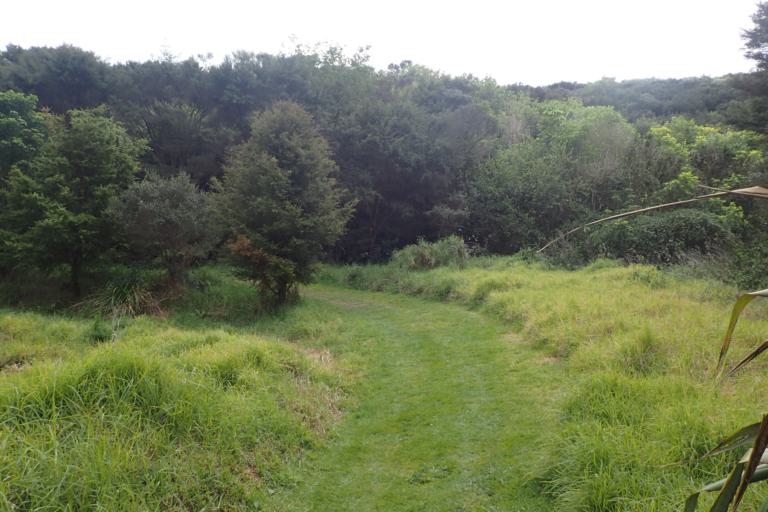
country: NZ
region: Auckland
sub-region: Auckland
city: Pakuranga
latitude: -36.7848
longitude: 174.9986
